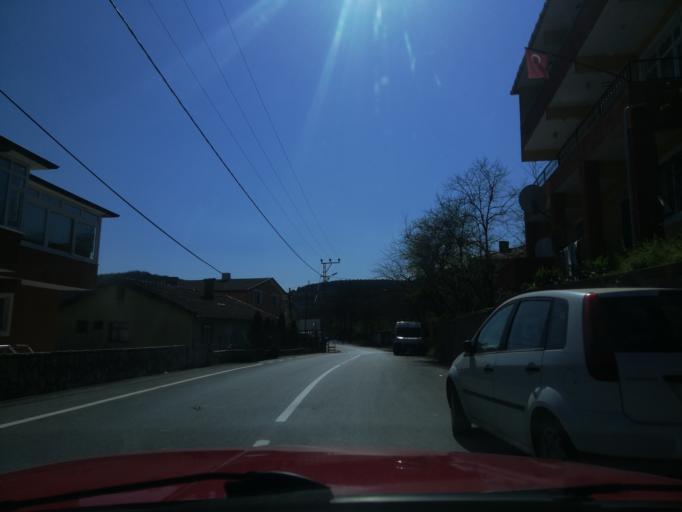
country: TR
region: Istanbul
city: Mahmut Sevket Pasa
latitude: 41.1269
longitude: 29.1587
